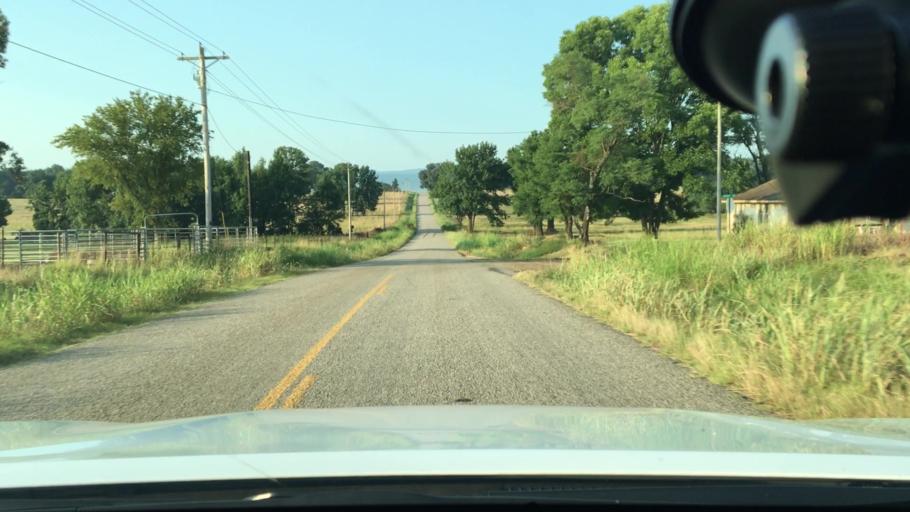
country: US
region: Arkansas
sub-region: Johnson County
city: Coal Hill
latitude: 35.3565
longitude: -93.6132
